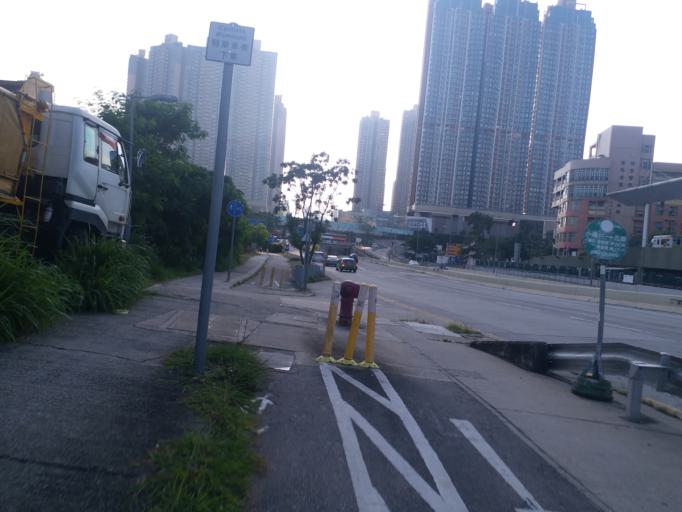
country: HK
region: Yuen Long
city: Yuen Long Kau Hui
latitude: 22.4442
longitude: 114.0422
